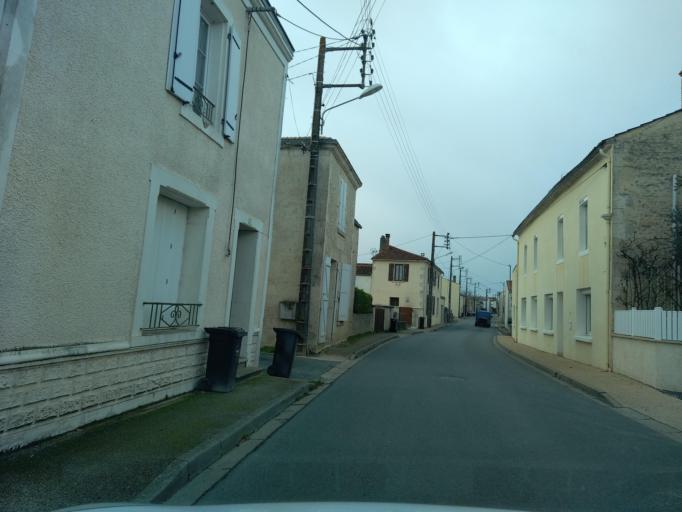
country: FR
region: Pays de la Loire
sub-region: Departement de la Vendee
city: Vix
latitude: 46.3649
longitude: -0.8610
